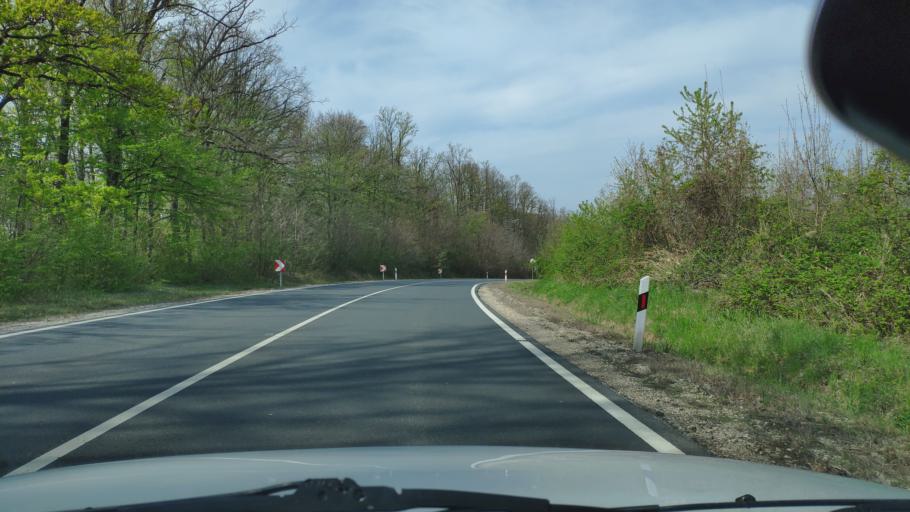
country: HU
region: Zala
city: Nagykanizsa
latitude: 46.4291
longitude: 17.0401
